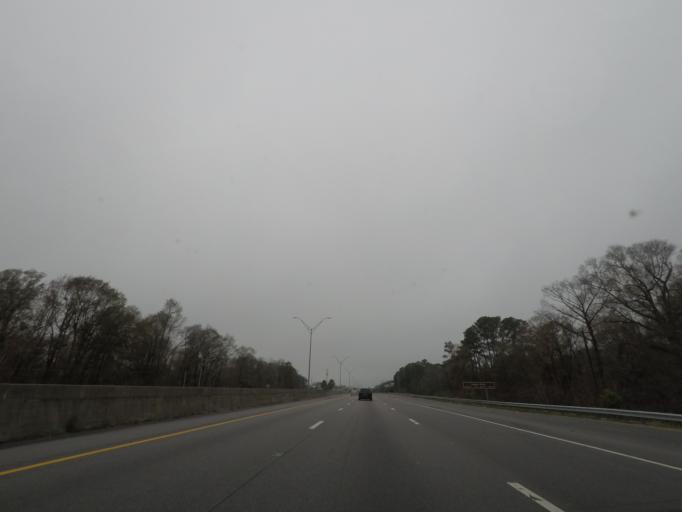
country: US
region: North Carolina
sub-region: Robeson County
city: Lumberton
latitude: 34.6330
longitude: -79.0283
